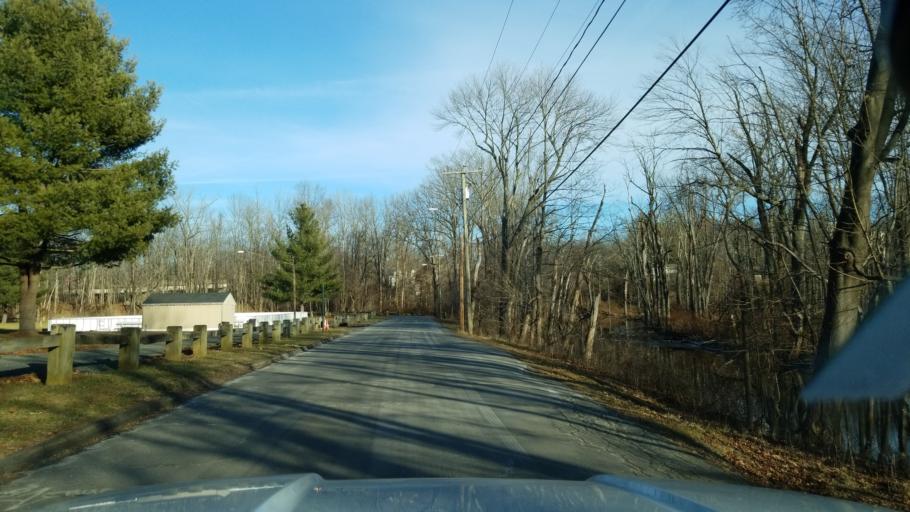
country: US
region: Connecticut
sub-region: Middlesex County
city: Middletown
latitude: 41.5595
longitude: -72.6682
